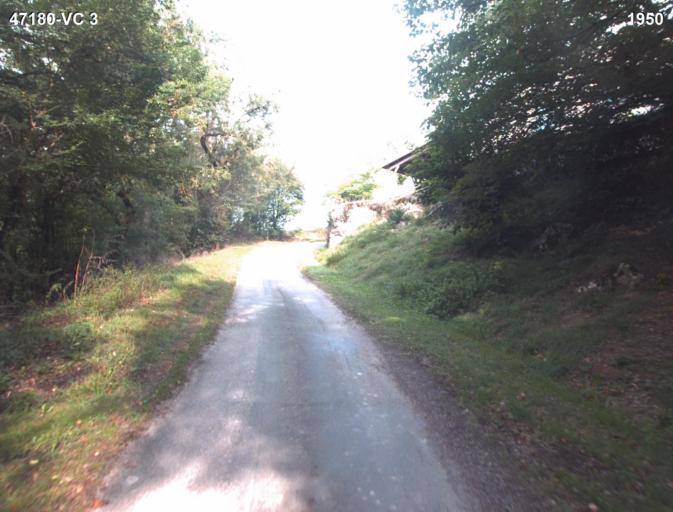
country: FR
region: Aquitaine
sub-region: Departement du Lot-et-Garonne
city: Sainte-Colombe-en-Bruilhois
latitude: 44.1531
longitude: 0.4411
